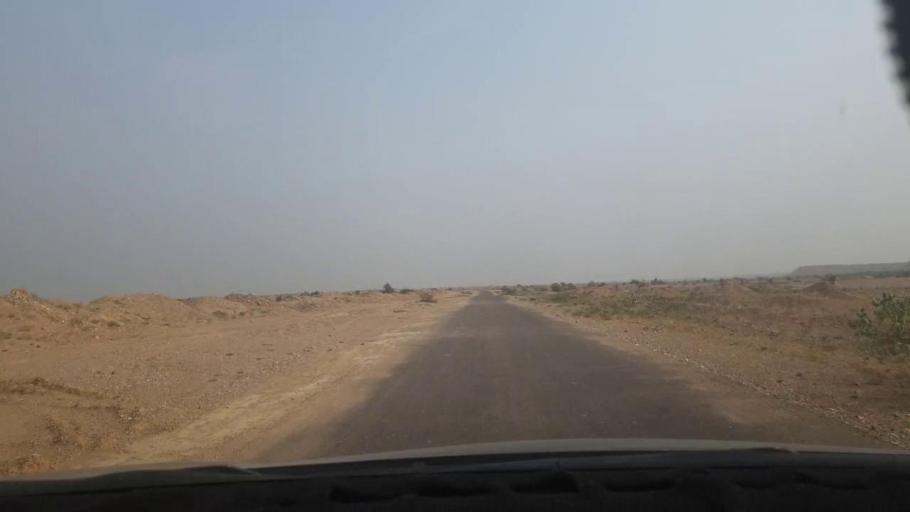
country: PK
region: Sindh
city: Matiari
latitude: 25.5794
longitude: 68.3155
